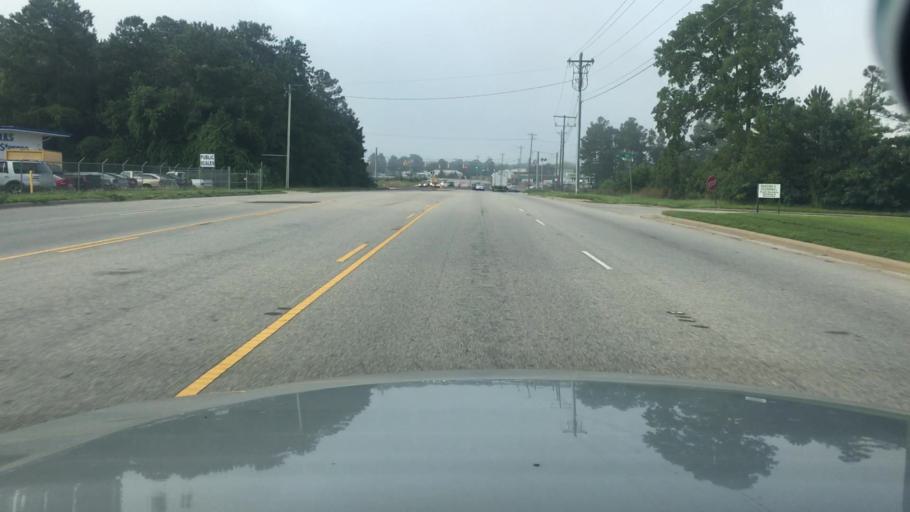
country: US
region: North Carolina
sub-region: Cumberland County
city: Hope Mills
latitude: 35.0102
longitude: -78.9189
